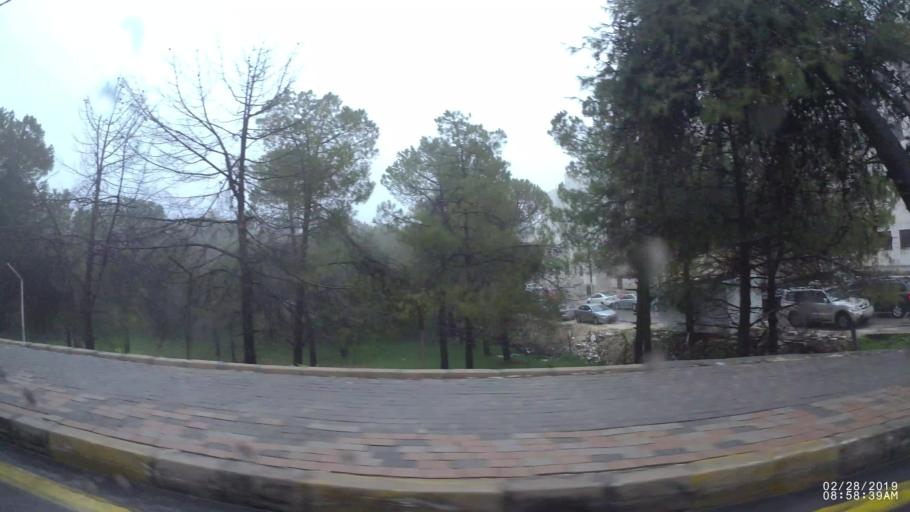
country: JO
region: Amman
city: Al Jubayhah
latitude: 32.0212
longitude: 35.8763
